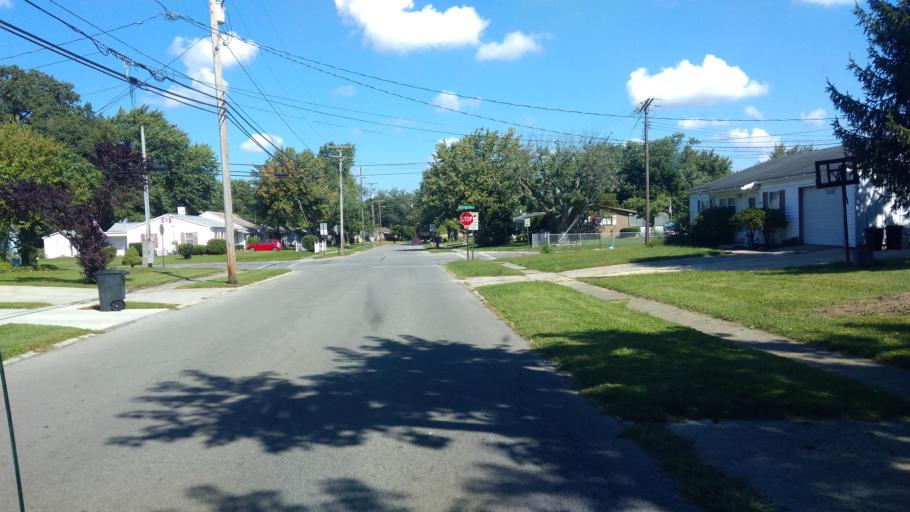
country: US
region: Ohio
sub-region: Marion County
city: Marion
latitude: 40.6064
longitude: -83.1201
